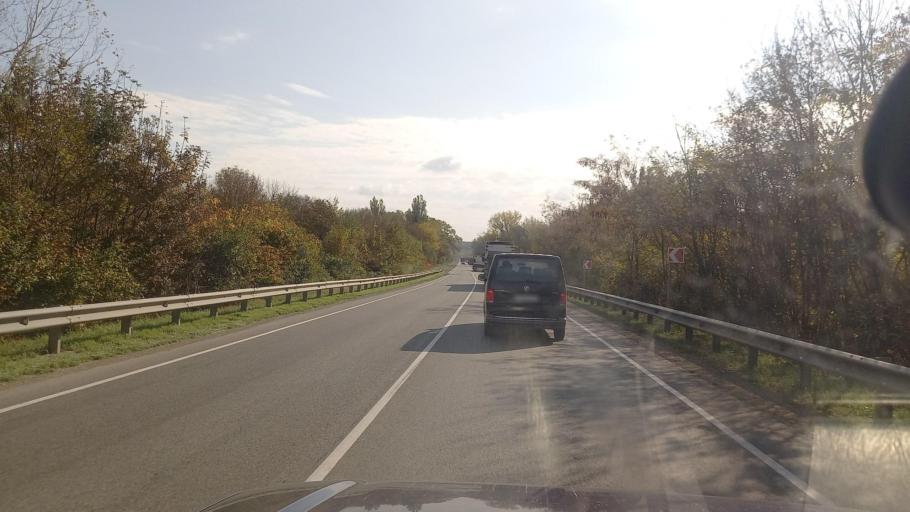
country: RU
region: Krasnodarskiy
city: Abinsk
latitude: 44.8444
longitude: 38.1527
